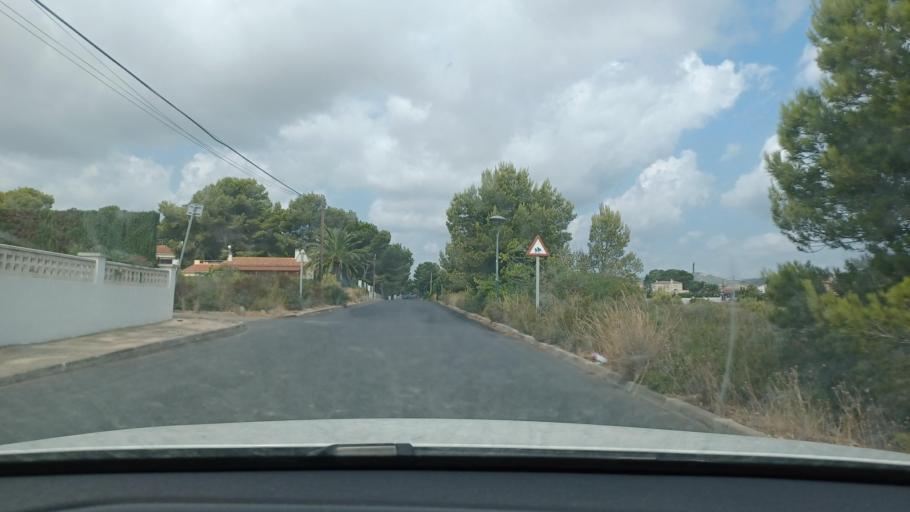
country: ES
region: Catalonia
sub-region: Provincia de Tarragona
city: l'Ametlla de Mar
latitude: 40.9064
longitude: 0.8144
